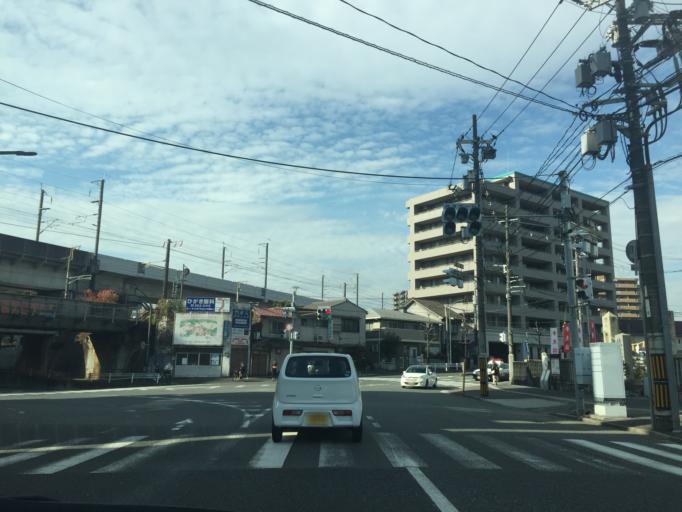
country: JP
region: Hiroshima
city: Hiroshima-shi
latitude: 34.4035
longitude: 132.4697
